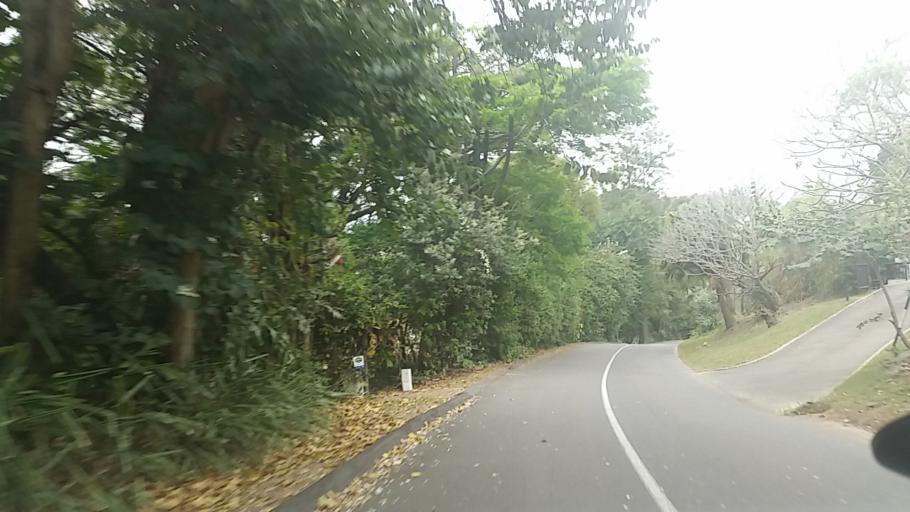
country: ZA
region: KwaZulu-Natal
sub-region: eThekwini Metropolitan Municipality
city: Berea
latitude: -29.8402
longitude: 30.9353
